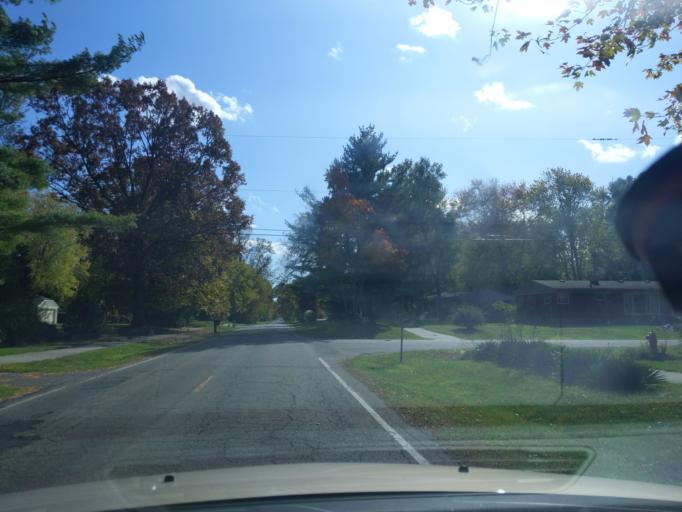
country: US
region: Michigan
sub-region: Ingham County
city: Haslett
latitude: 42.7451
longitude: -84.3931
